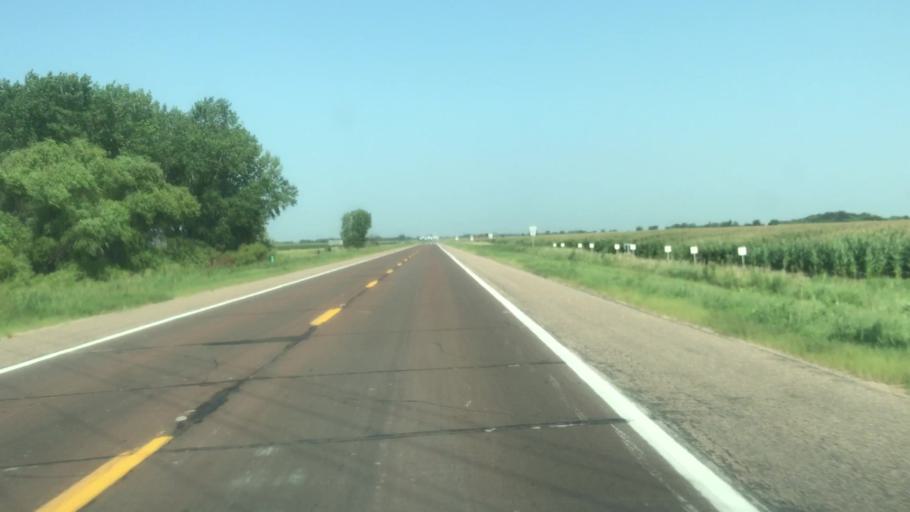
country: US
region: Nebraska
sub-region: Hall County
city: Grand Island
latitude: 40.9751
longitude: -98.5120
